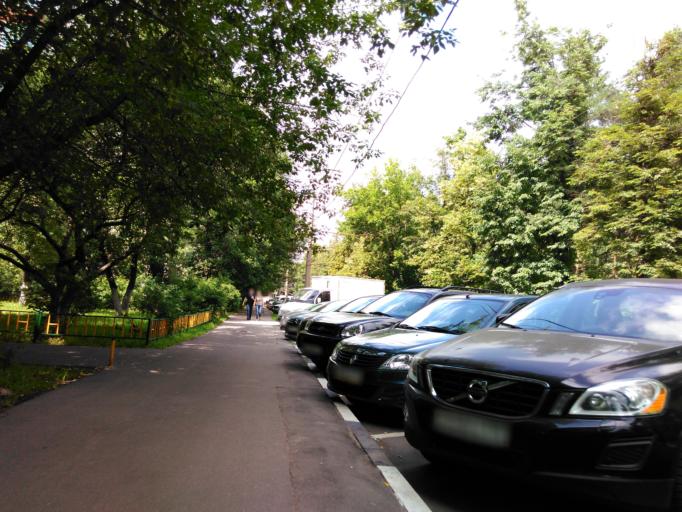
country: RU
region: Moscow
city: Ramenki
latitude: 55.6823
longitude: 37.5218
